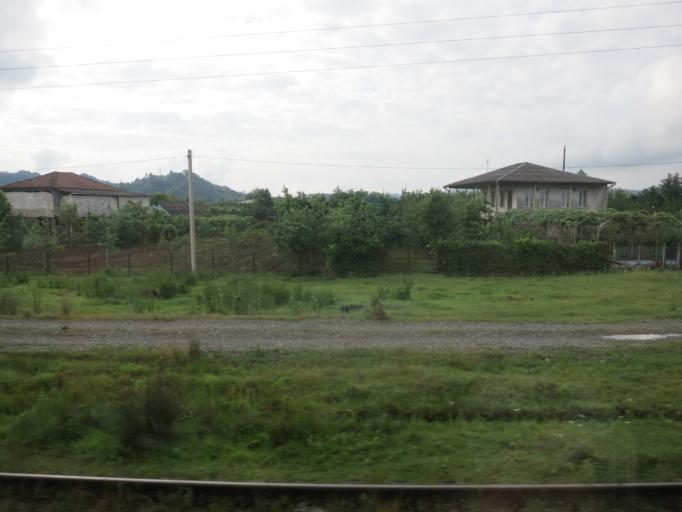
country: GE
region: Guria
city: Urek'i
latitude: 42.0469
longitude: 41.8165
